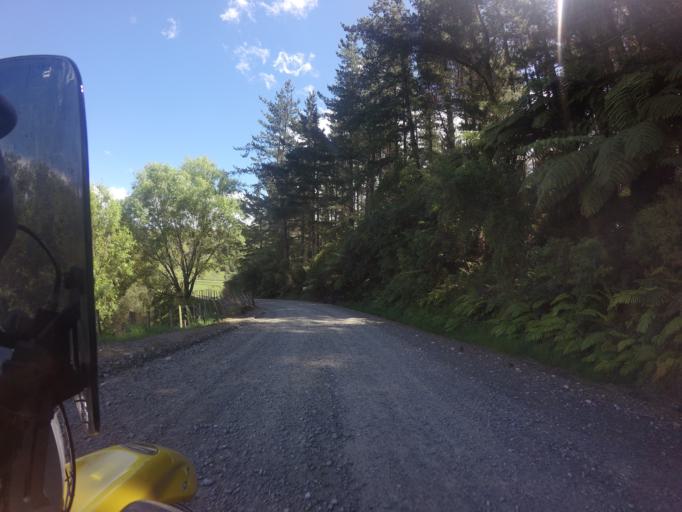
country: NZ
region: Hawke's Bay
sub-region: Wairoa District
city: Wairoa
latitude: -38.9830
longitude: 177.7025
